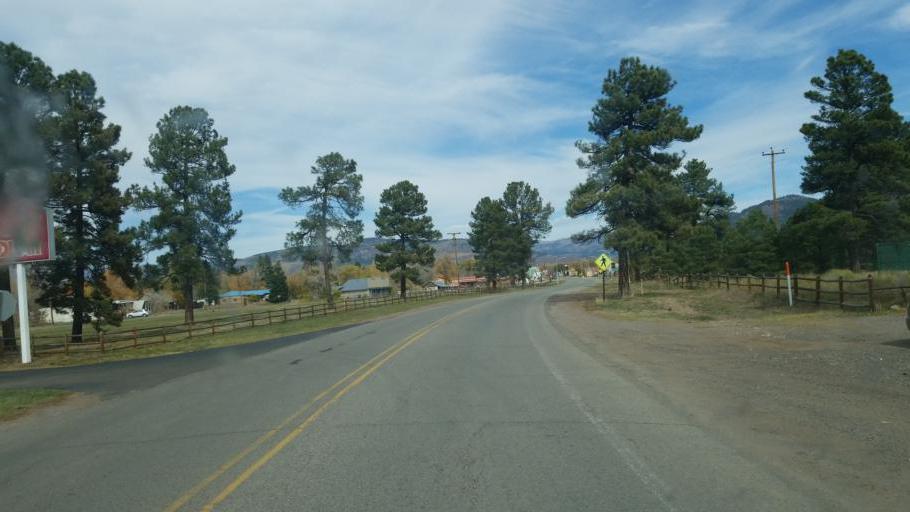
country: US
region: New Mexico
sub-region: Rio Arriba County
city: Chama
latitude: 36.8984
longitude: -106.5817
